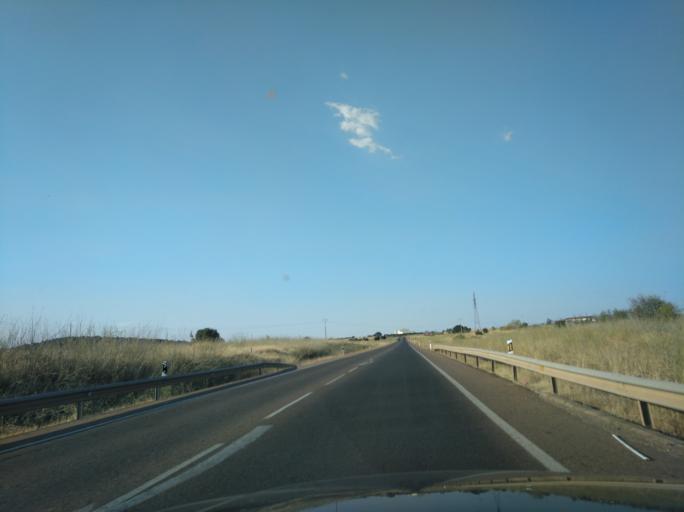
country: ES
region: Extremadura
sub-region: Provincia de Badajoz
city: Olivenza
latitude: 38.6989
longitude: -7.0894
